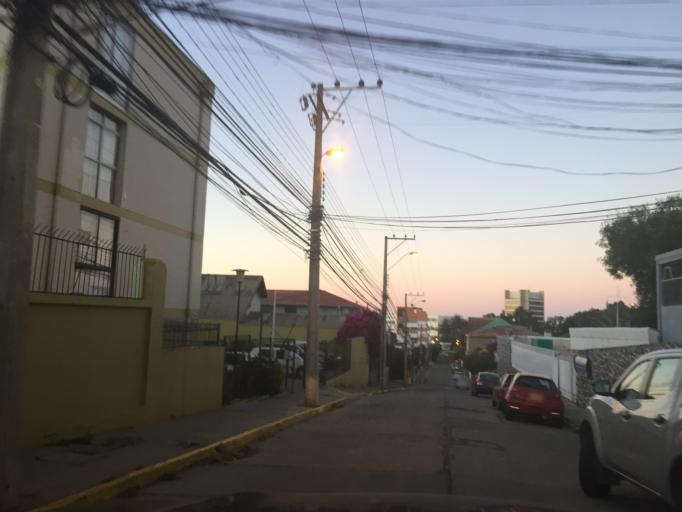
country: CL
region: Valparaiso
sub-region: Provincia de Valparaiso
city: Valparaiso
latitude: -33.0253
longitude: -71.6371
